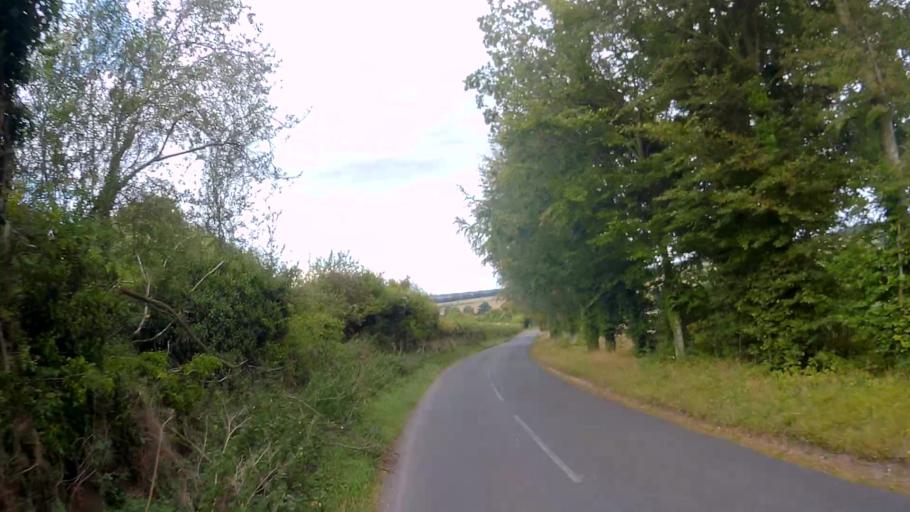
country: GB
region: England
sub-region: Hampshire
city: Kings Worthy
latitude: 51.1371
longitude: -1.1948
